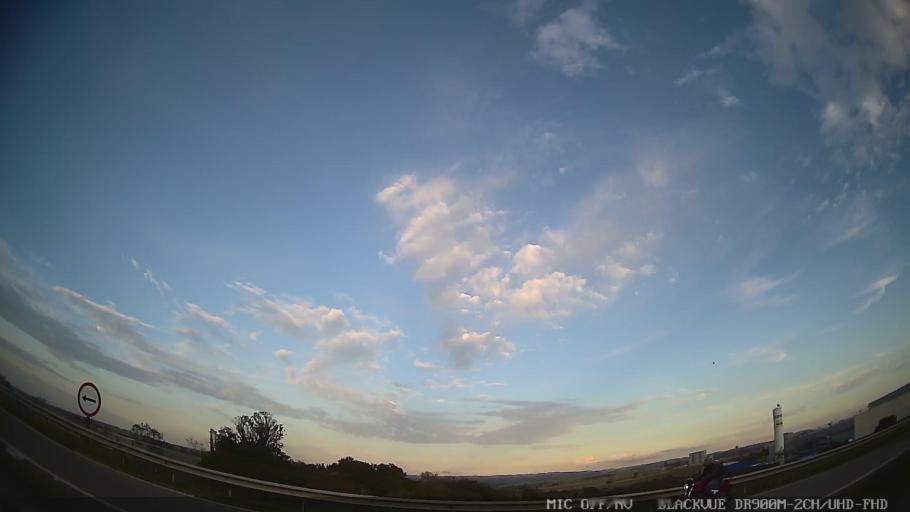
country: BR
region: Sao Paulo
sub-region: Salto
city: Salto
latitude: -23.1684
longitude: -47.2675
